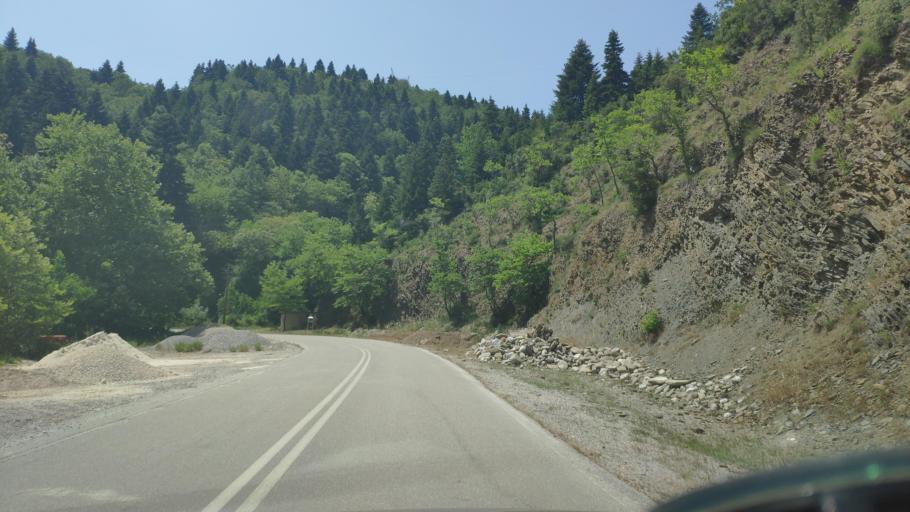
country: GR
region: Epirus
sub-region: Nomos Artas
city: Ano Kalentini
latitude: 39.2749
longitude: 21.2899
